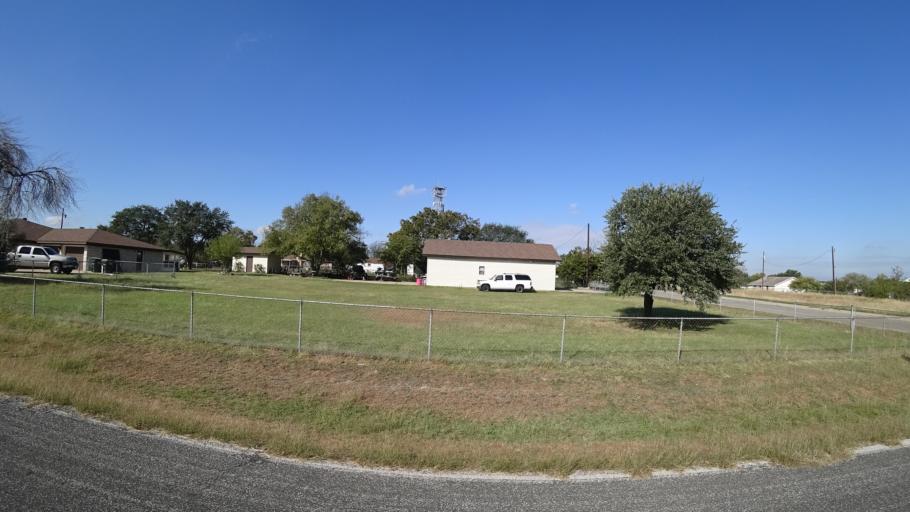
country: US
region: Texas
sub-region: Travis County
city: Windemere
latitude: 30.4434
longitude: -97.6509
